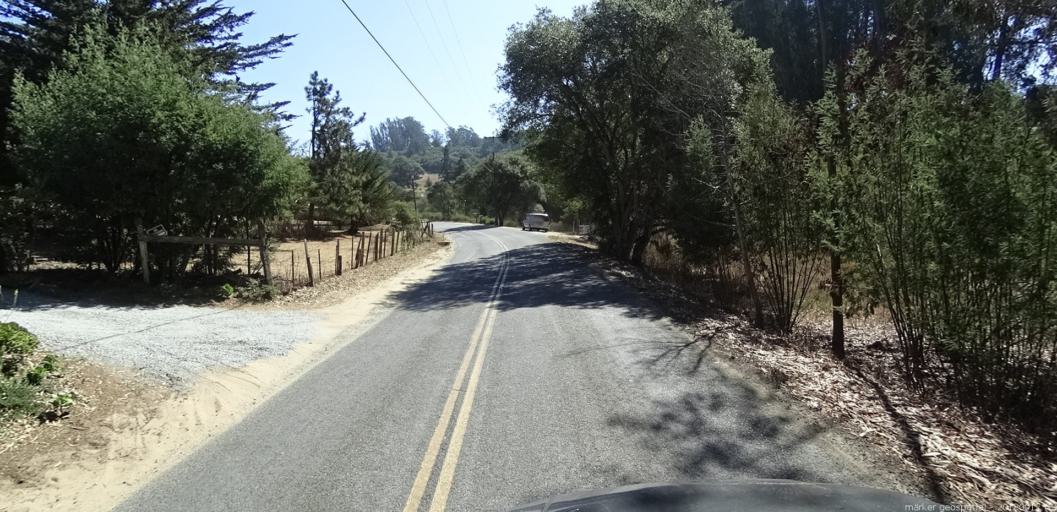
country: US
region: California
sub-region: Monterey County
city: Elkhorn
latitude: 36.8252
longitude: -121.7234
